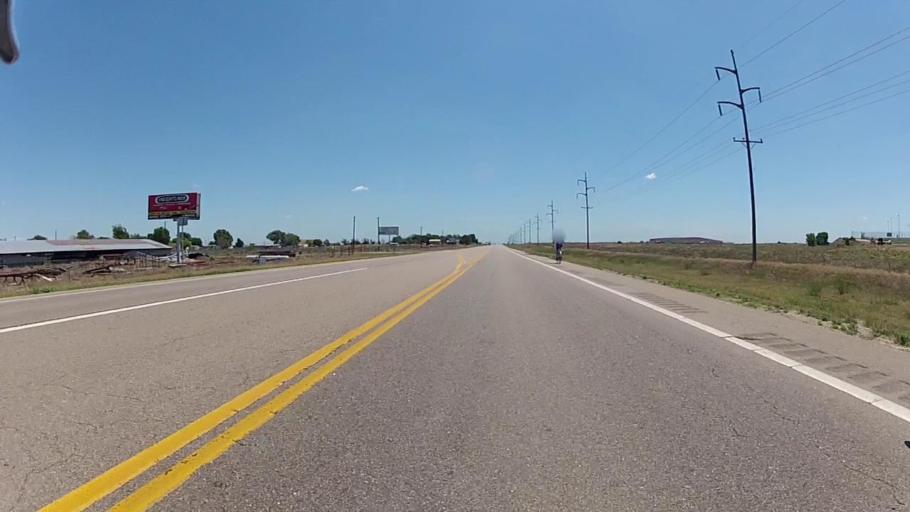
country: US
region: Kansas
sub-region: Ford County
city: Dodge City
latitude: 37.7218
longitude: -100.0317
